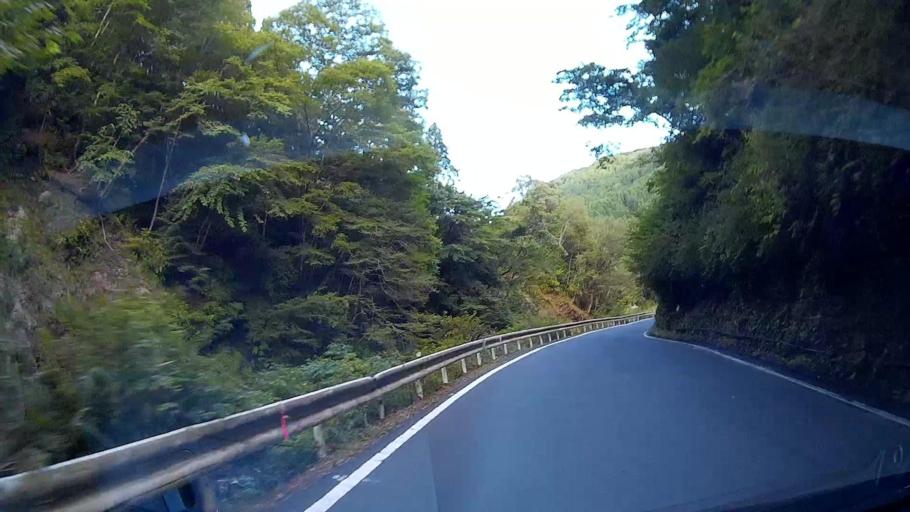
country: JP
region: Shizuoka
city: Shizuoka-shi
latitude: 35.1541
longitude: 138.2566
